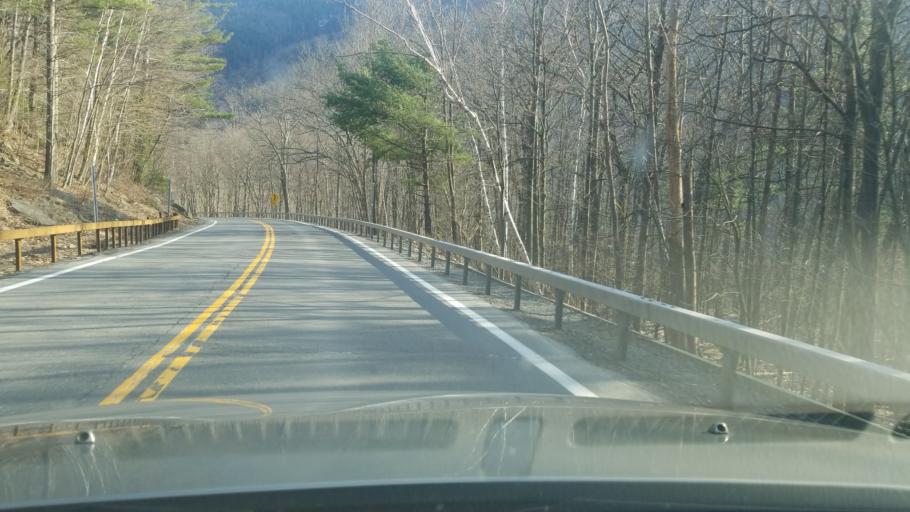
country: US
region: New York
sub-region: Greene County
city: Palenville
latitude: 42.1875
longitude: -74.0721
